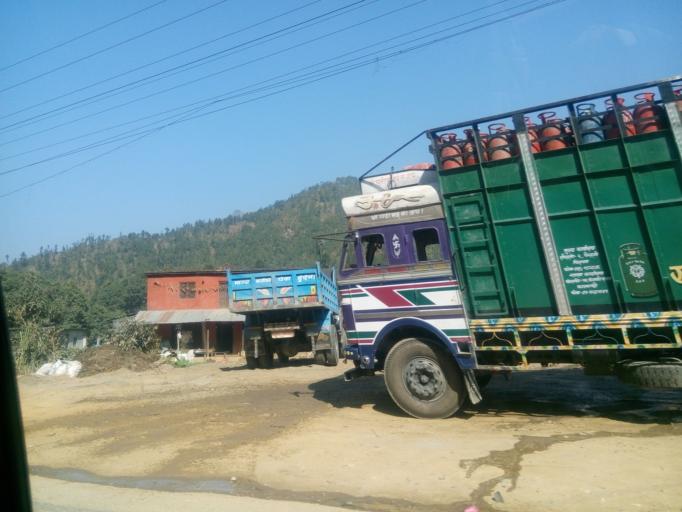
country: NP
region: Central Region
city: Kirtipur
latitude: 27.7667
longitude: 85.0409
